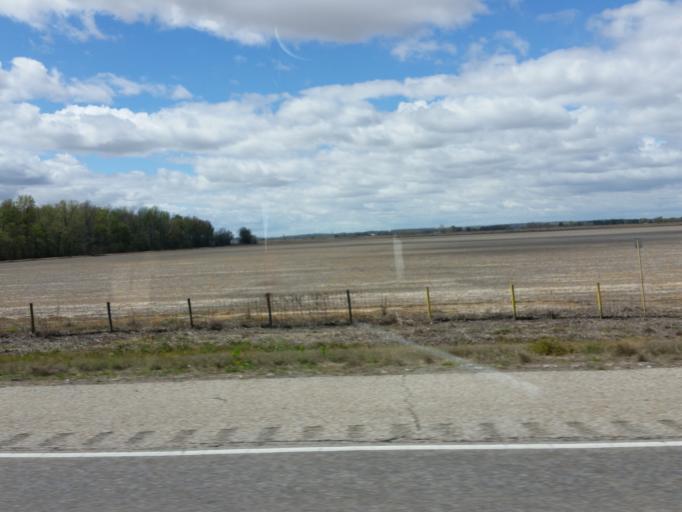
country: US
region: Arkansas
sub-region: Craighead County
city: Bay
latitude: 35.7210
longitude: -90.5801
